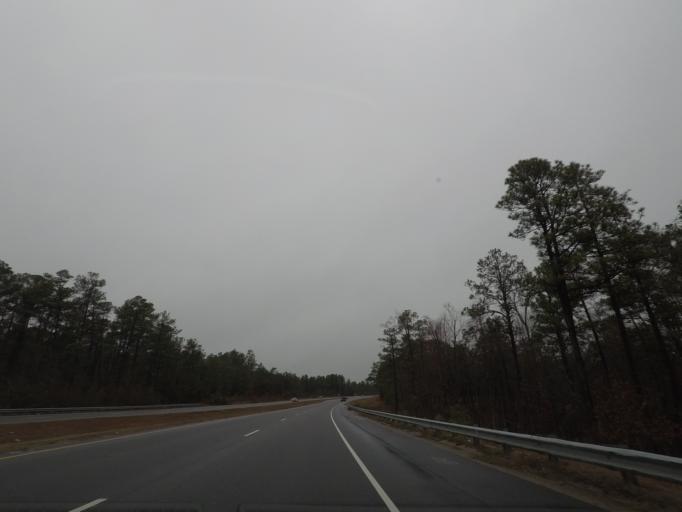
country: US
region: North Carolina
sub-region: Cumberland County
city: Spring Lake
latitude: 35.2331
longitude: -79.0183
